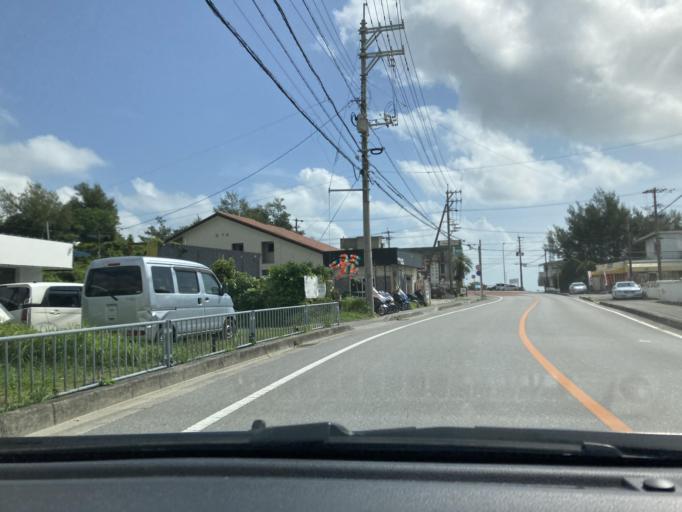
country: JP
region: Okinawa
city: Okinawa
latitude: 26.3201
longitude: 127.8067
